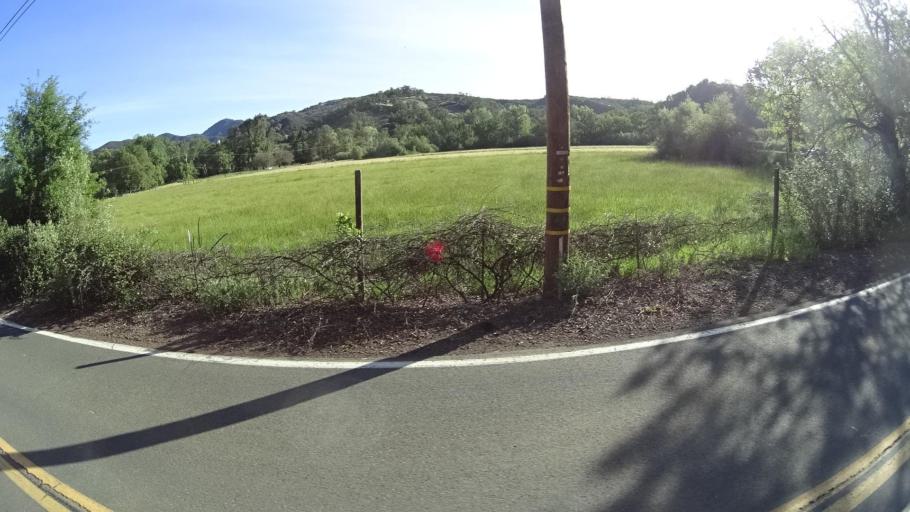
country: US
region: California
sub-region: Lake County
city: North Lakeport
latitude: 39.1147
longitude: -122.9850
